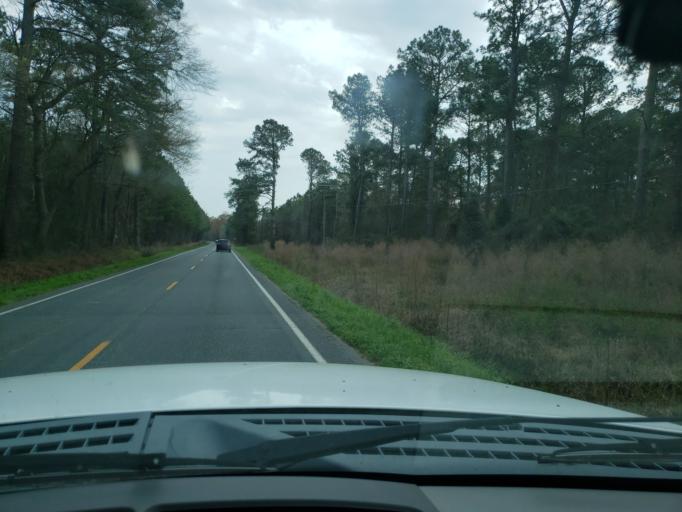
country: US
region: North Carolina
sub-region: Duplin County
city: Wallace
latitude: 34.7938
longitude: -77.8599
